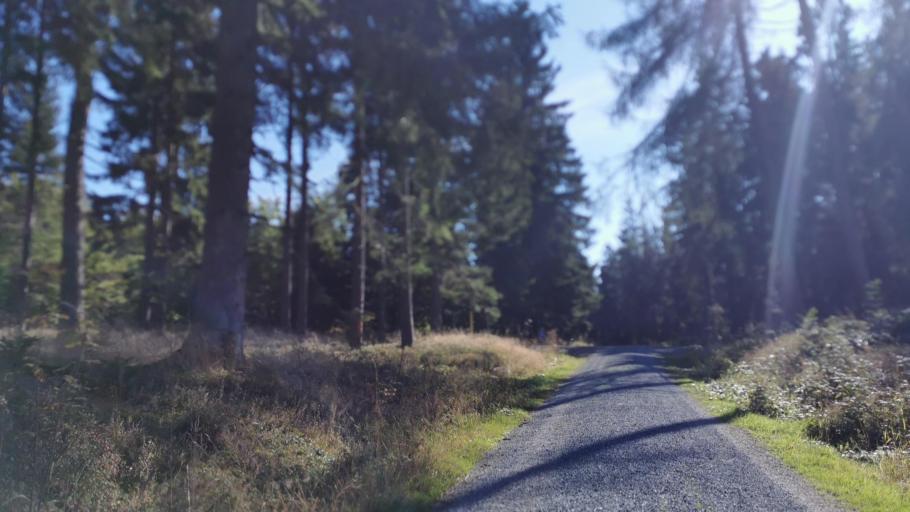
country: DE
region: Bavaria
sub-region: Upper Franconia
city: Ludwigsstadt
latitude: 50.4456
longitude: 11.3527
